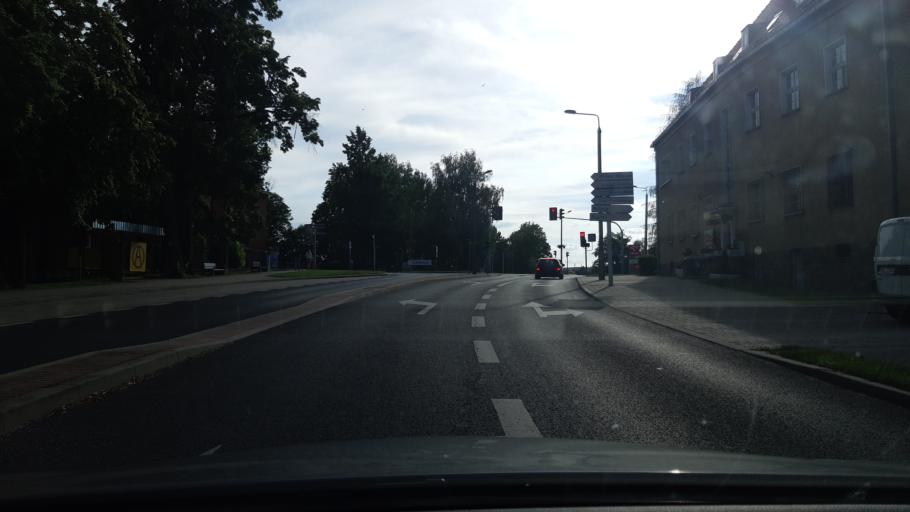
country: PL
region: Warmian-Masurian Voivodeship
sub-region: Powiat mragowski
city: Mragowo
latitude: 53.8770
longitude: 21.3053
